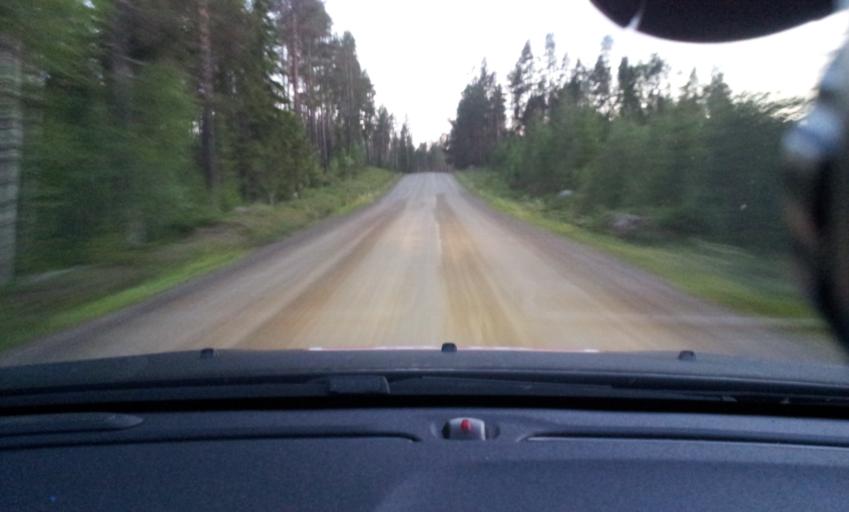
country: SE
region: Vaesternorrland
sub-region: Ange Kommun
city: Ange
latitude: 62.7670
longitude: 15.8334
